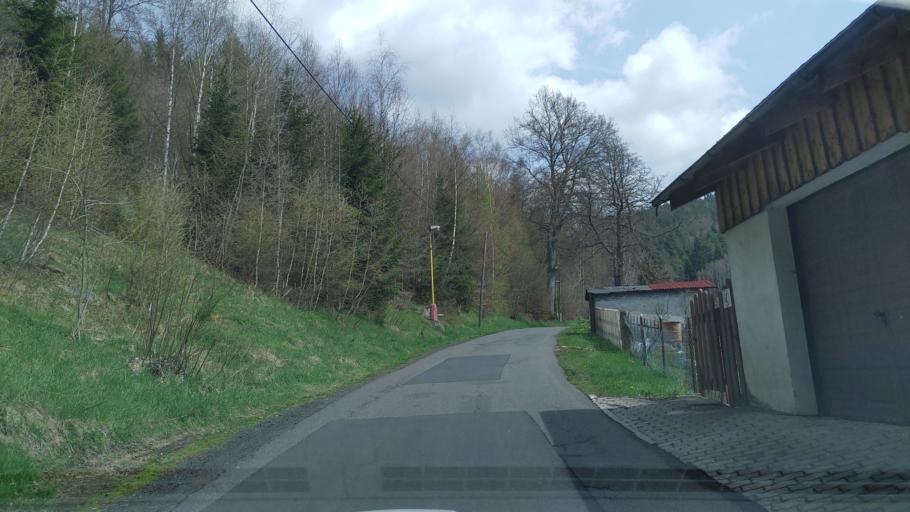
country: CZ
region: Karlovarsky
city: Jachymov
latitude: 50.3592
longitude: 12.9400
